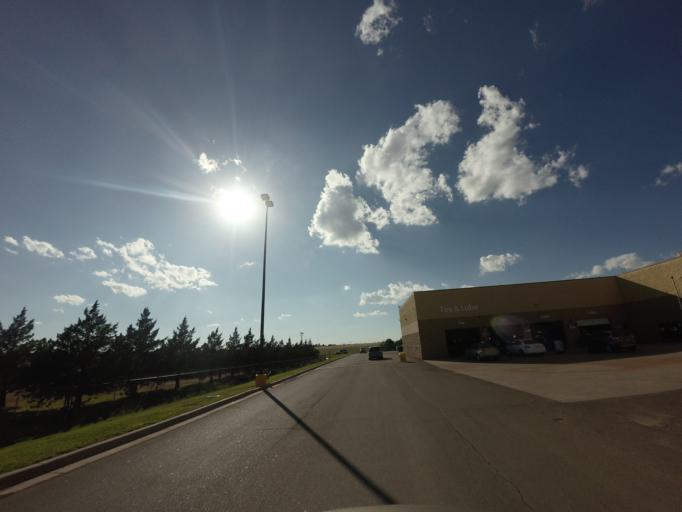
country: US
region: New Mexico
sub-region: Curry County
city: Clovis
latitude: 34.4367
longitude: -103.2002
